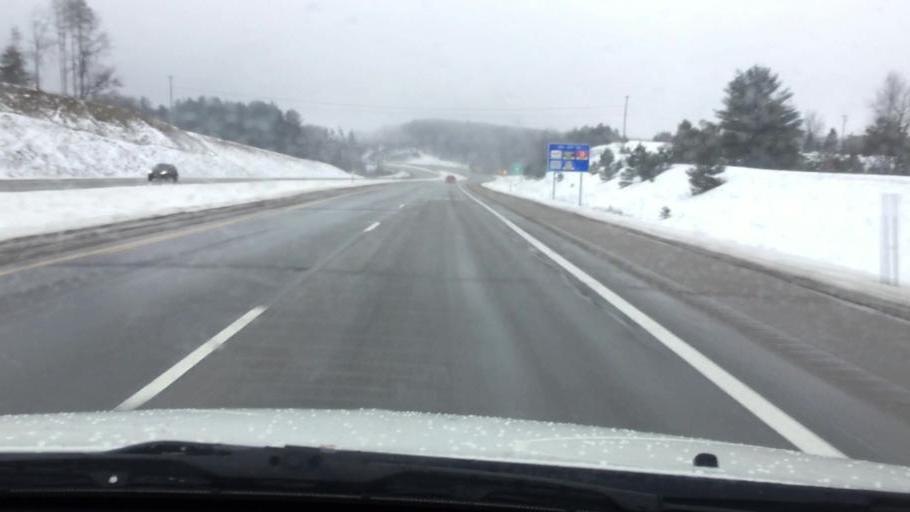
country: US
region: Michigan
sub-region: Wexford County
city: Cadillac
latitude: 44.3046
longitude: -85.3925
